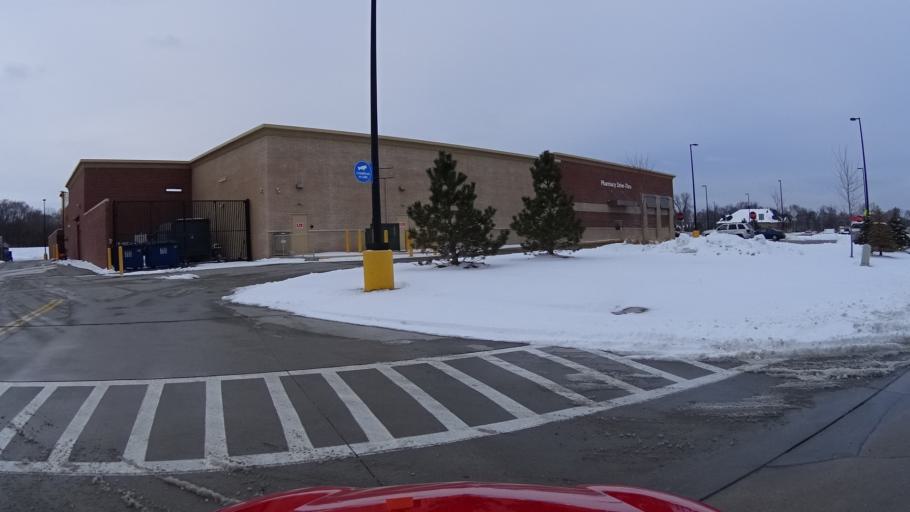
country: US
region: Nebraska
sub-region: Sarpy County
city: Offutt Air Force Base
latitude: 41.1159
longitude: -95.9421
